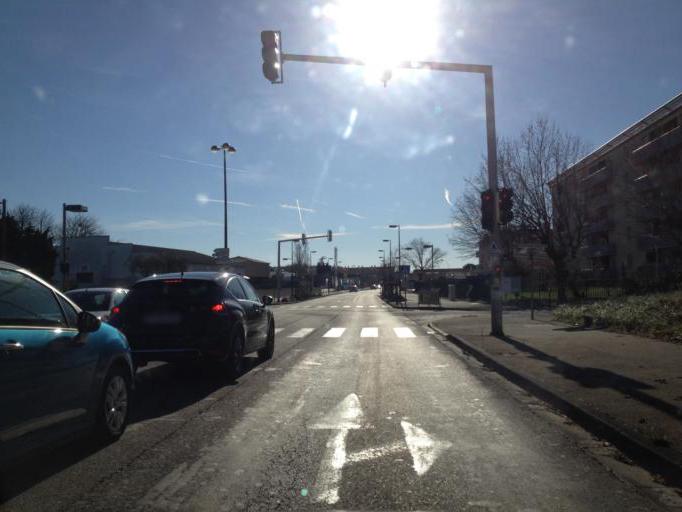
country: FR
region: Provence-Alpes-Cote d'Azur
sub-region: Departement du Vaucluse
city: Orange
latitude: 44.1527
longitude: 4.8028
